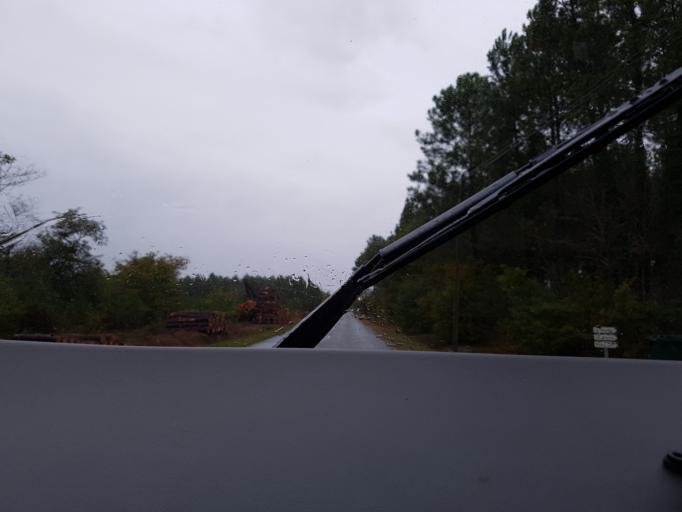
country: FR
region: Aquitaine
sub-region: Departement de la Gironde
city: Saint-Symphorien
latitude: 44.3530
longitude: -0.6232
